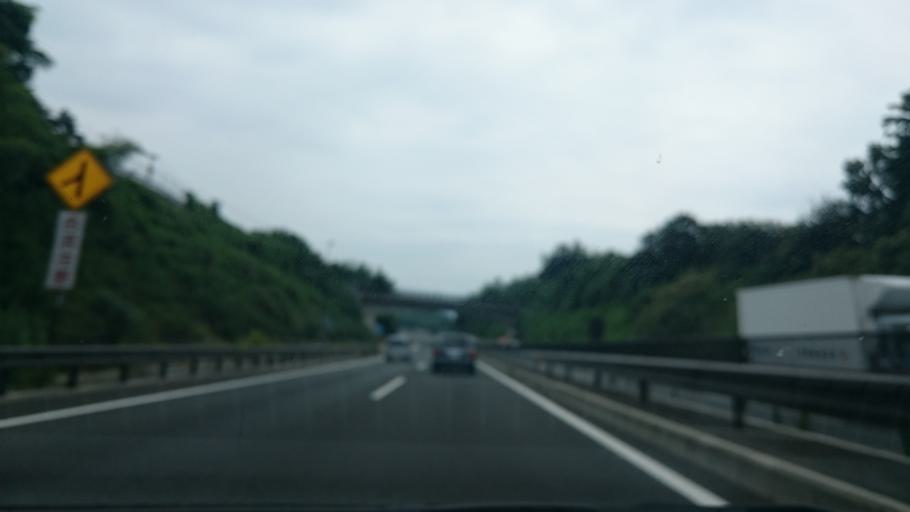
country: JP
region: Shizuoka
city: Mishima
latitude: 35.1391
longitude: 138.9386
